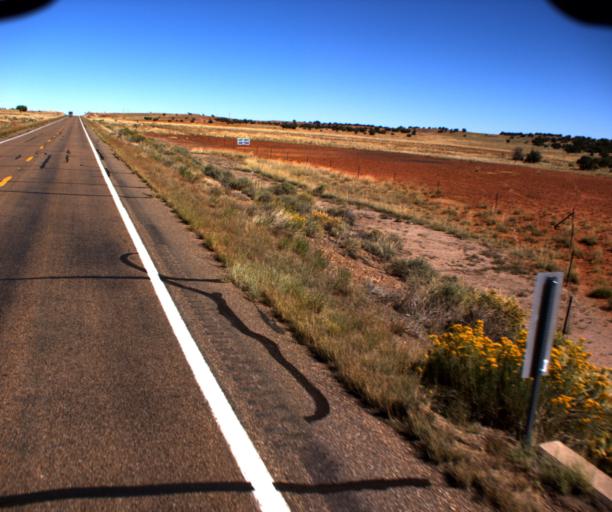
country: US
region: Arizona
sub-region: Apache County
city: Saint Johns
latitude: 34.4565
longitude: -109.4042
